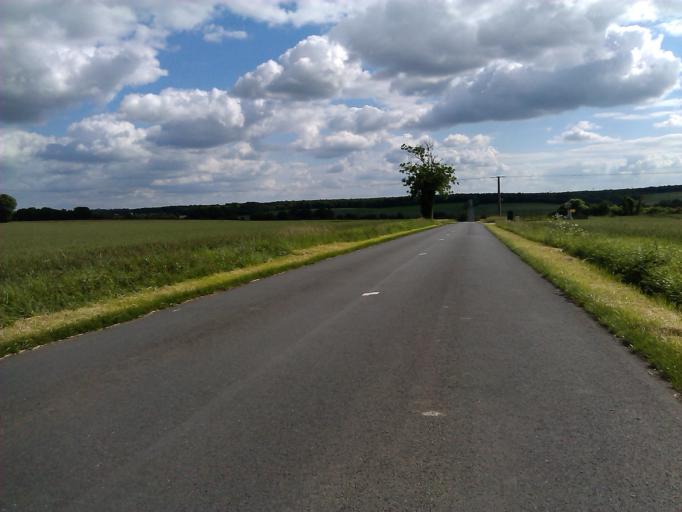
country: FR
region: Poitou-Charentes
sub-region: Departement de la Charente
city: Mansle
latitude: 45.8650
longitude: 0.1707
